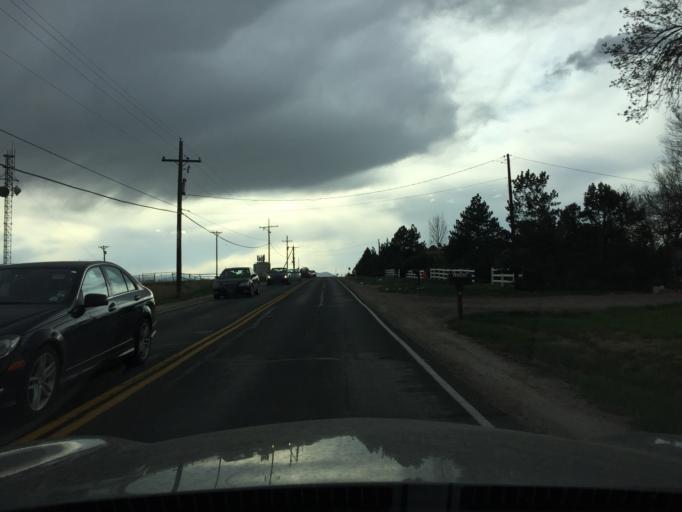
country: US
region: Colorado
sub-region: Broomfield County
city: Broomfield
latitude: 39.9578
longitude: -105.0577
